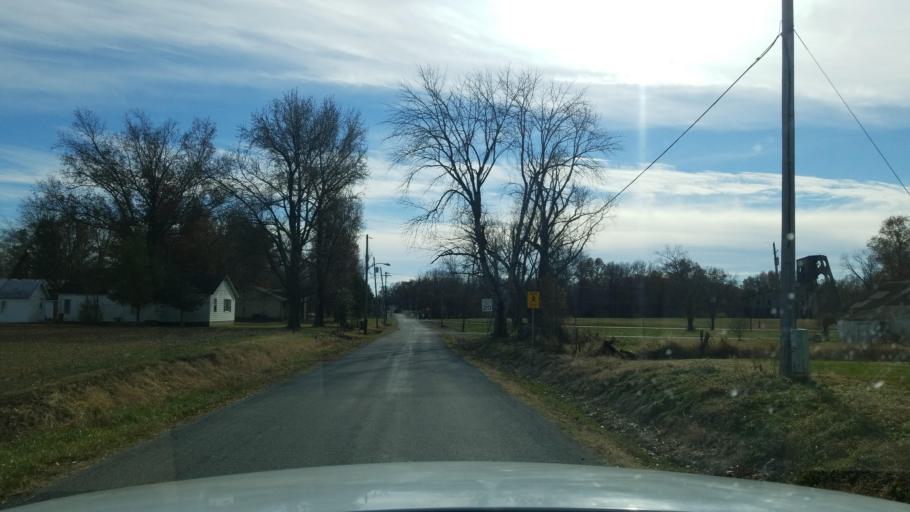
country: US
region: Illinois
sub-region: Saline County
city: Harrisburg
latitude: 37.7678
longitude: -88.5171
